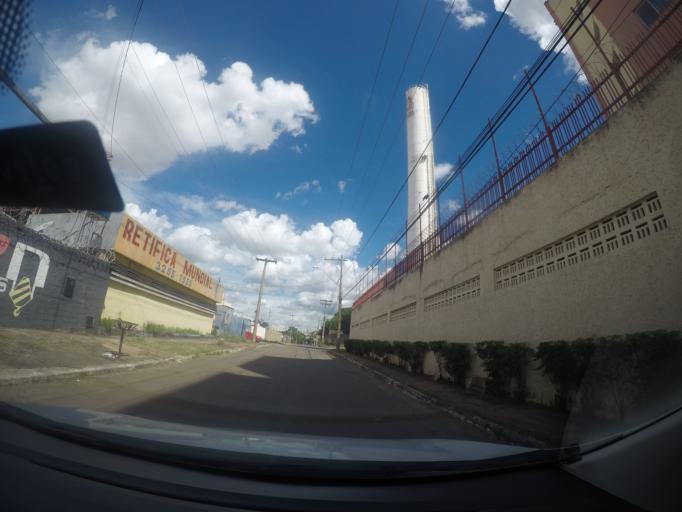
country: BR
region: Goias
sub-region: Goiania
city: Goiania
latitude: -16.6749
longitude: -49.2984
